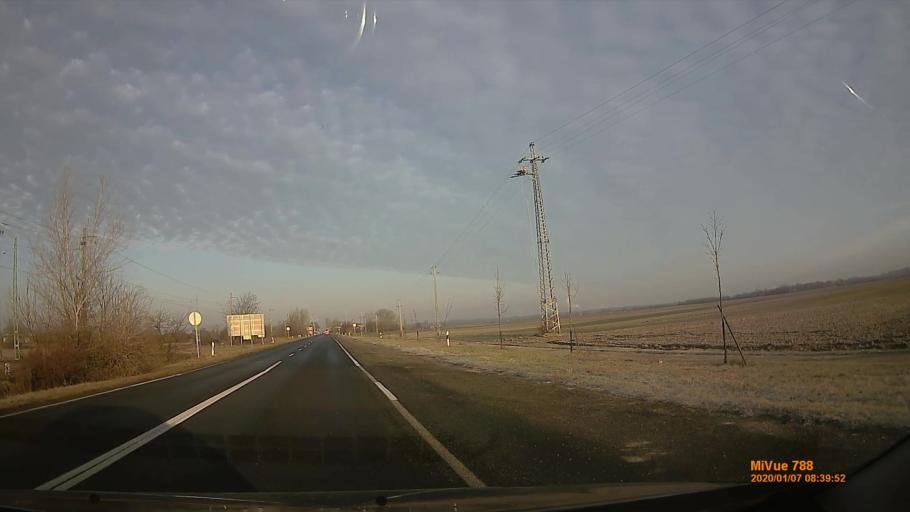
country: HU
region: Gyor-Moson-Sopron
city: Rajka
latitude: 48.0080
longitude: 17.1838
